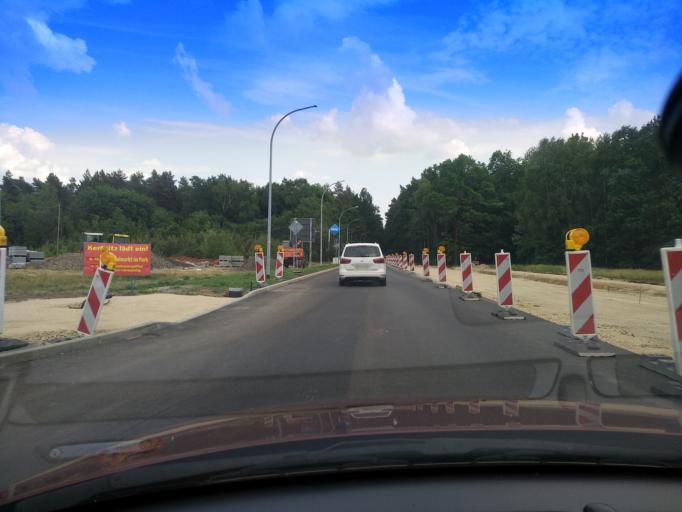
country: DE
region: Saxony
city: Niesky
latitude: 51.2793
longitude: 14.8184
